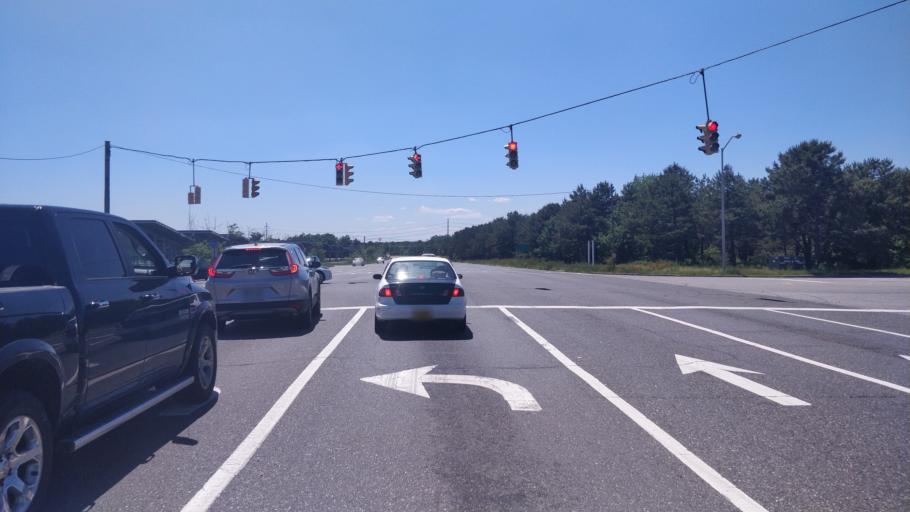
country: US
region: New York
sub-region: Suffolk County
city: Bay Wood
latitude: 40.7721
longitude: -73.2912
